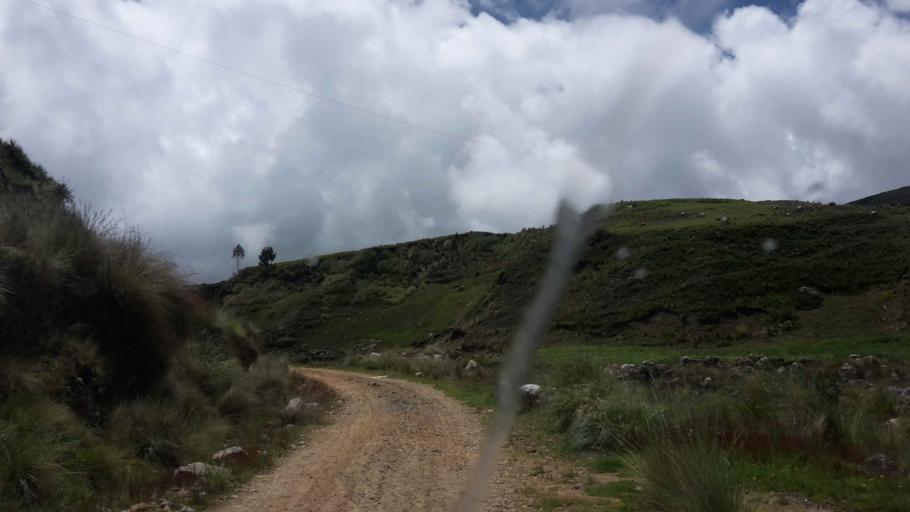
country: BO
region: Cochabamba
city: Cochabamba
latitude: -17.1824
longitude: -66.0611
